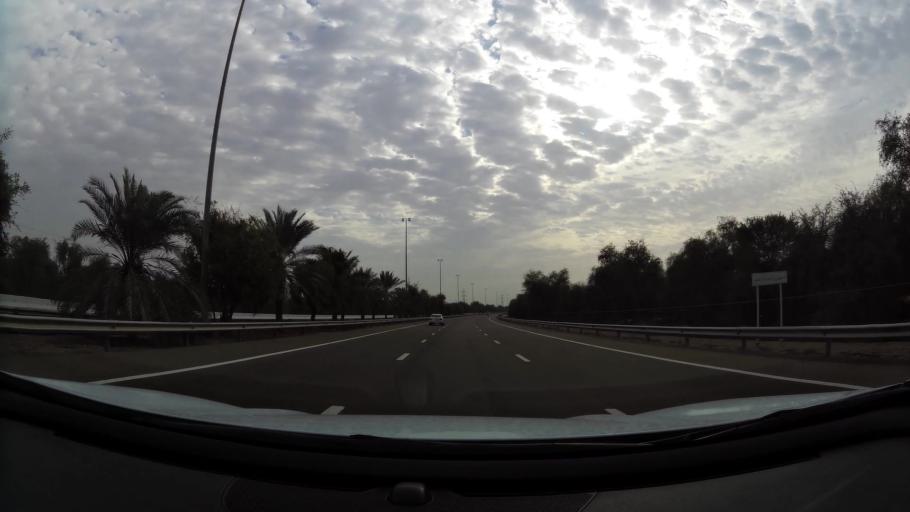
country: AE
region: Abu Dhabi
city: Al Ain
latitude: 24.1781
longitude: 55.1906
